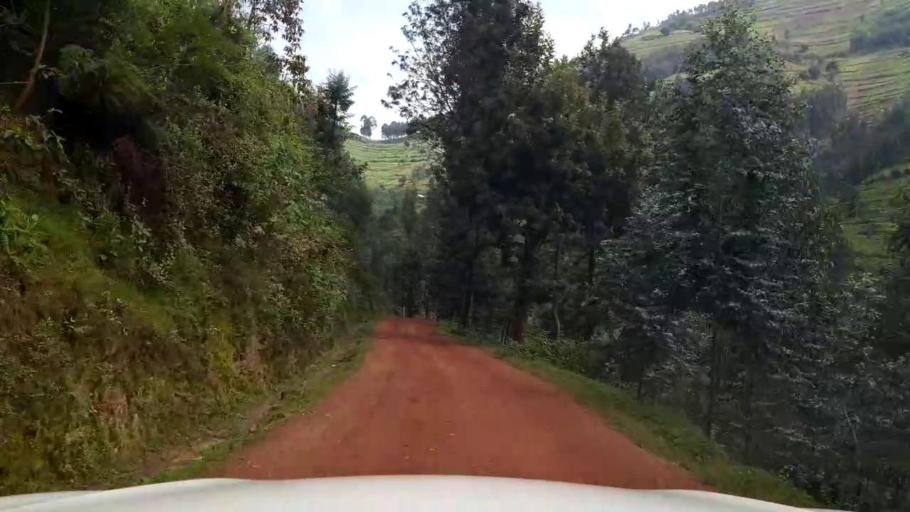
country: UG
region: Western Region
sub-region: Kisoro District
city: Kisoro
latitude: -1.3819
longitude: 29.7944
